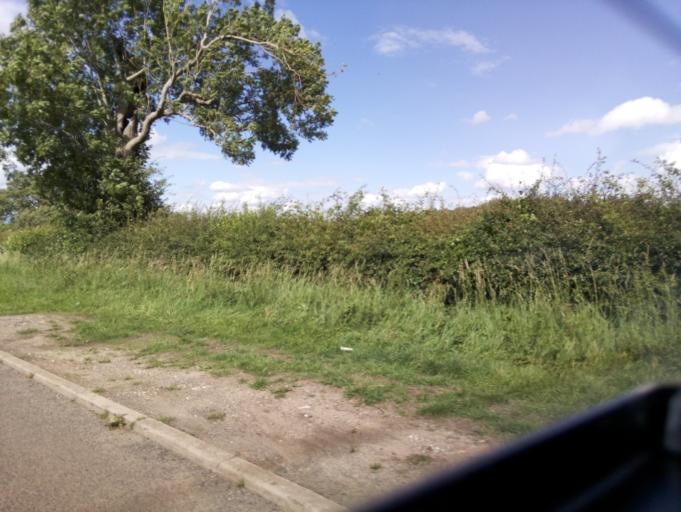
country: GB
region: England
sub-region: Nottinghamshire
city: East Leake
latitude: 52.8193
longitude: -1.2105
